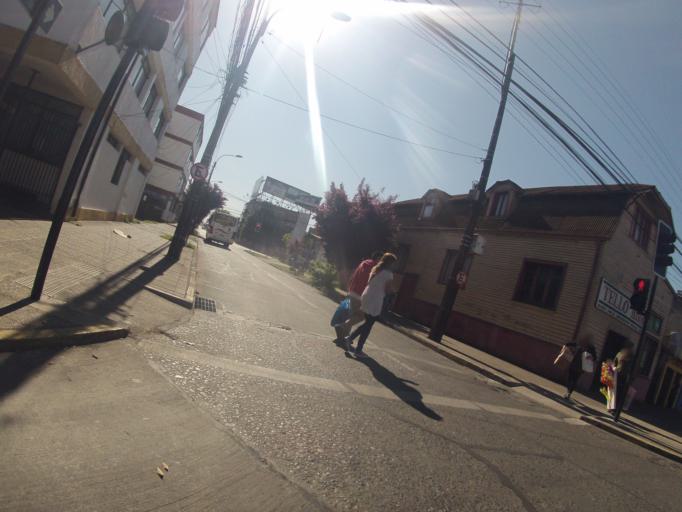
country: CL
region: Araucania
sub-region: Provincia de Cautin
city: Temuco
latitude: -38.7343
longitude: -72.5894
